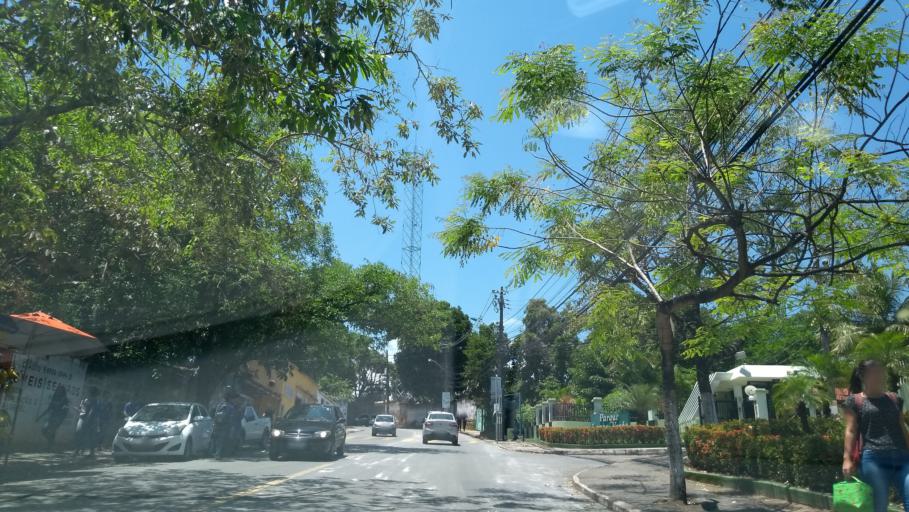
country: BR
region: Bahia
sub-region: Lauro De Freitas
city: Lauro de Freitas
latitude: -12.9381
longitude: -38.4142
